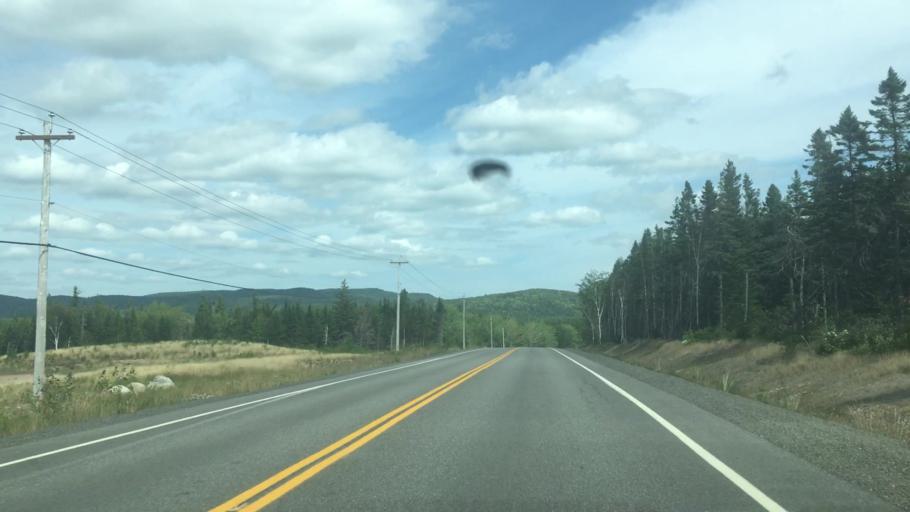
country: CA
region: Nova Scotia
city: Sydney Mines
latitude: 46.3307
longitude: -60.6011
